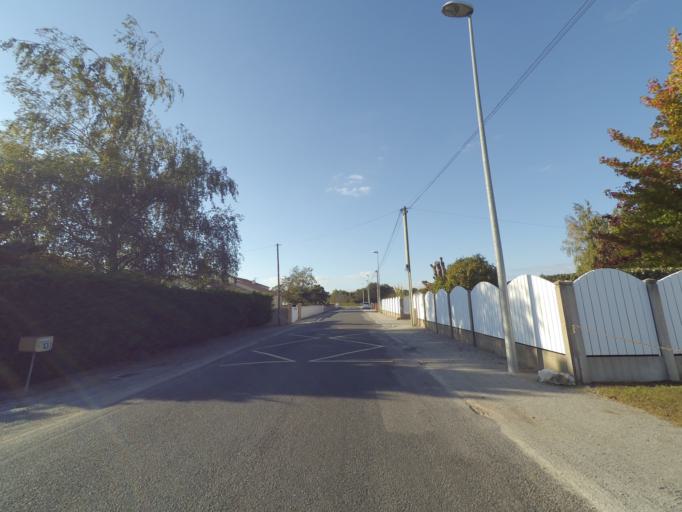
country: FR
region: Pays de la Loire
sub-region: Departement de la Loire-Atlantique
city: Chemere
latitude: 47.1286
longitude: -1.9242
